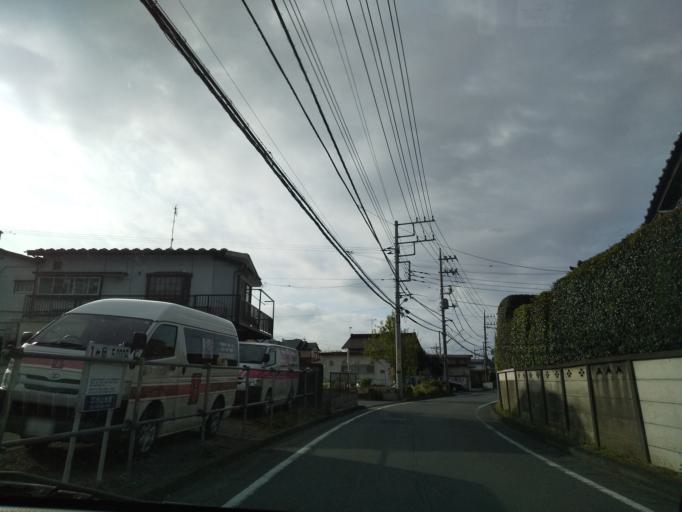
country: JP
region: Tokyo
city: Hachioji
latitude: 35.6880
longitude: 139.3090
